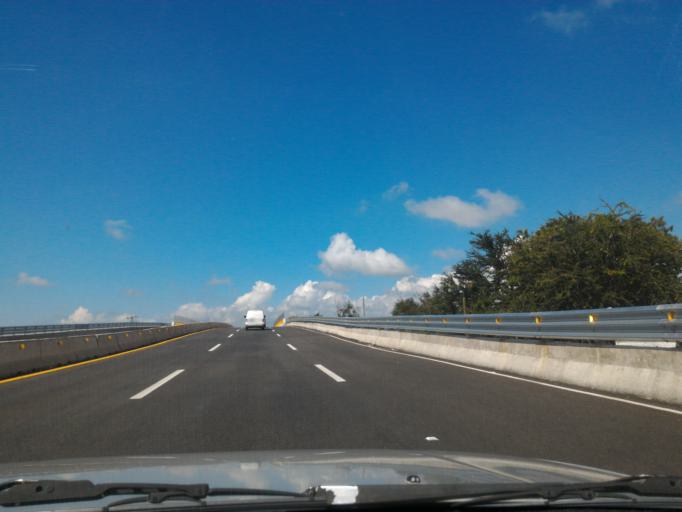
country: MX
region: Jalisco
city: La Venta del Astillero
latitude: 20.7322
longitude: -103.6094
